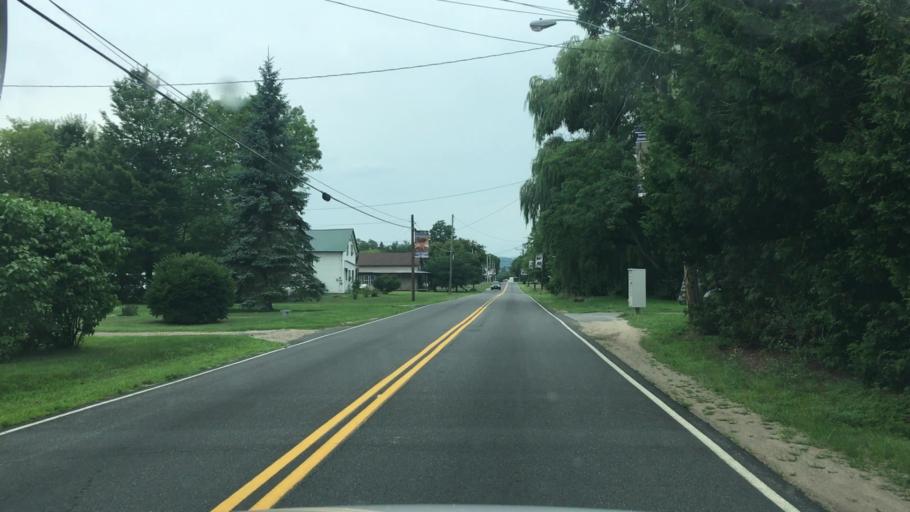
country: US
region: New York
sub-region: Essex County
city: Keeseville
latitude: 44.5008
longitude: -73.4711
